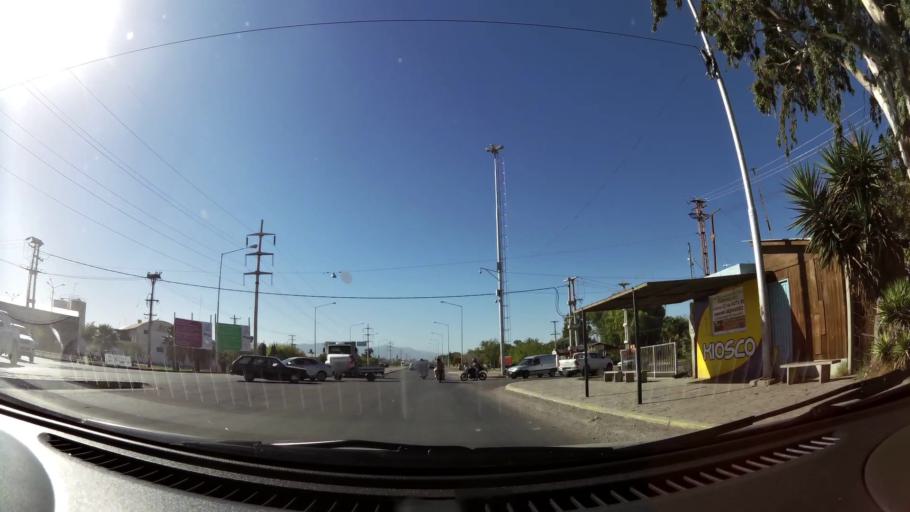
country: AR
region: San Juan
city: Villa Paula de Sarmiento
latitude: -31.5080
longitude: -68.5175
